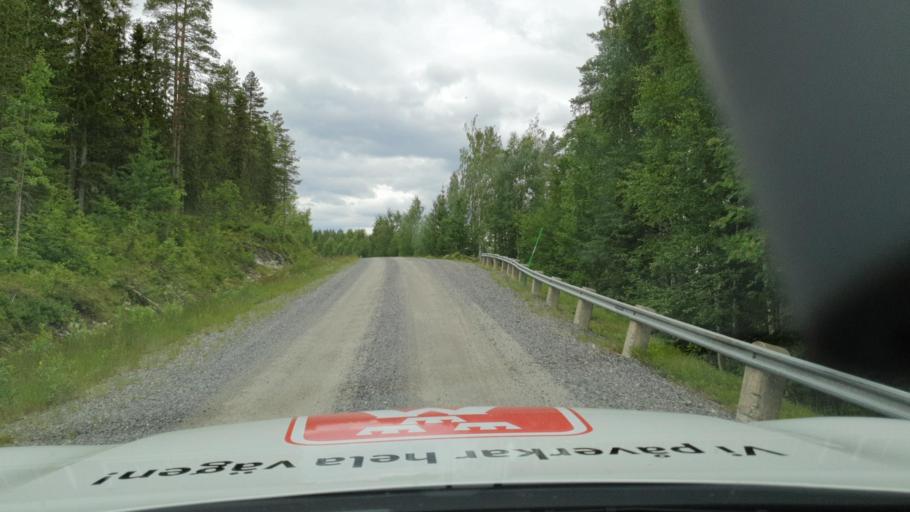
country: SE
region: Vaesterbotten
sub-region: Bjurholms Kommun
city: Bjurholm
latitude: 63.7585
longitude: 19.3667
